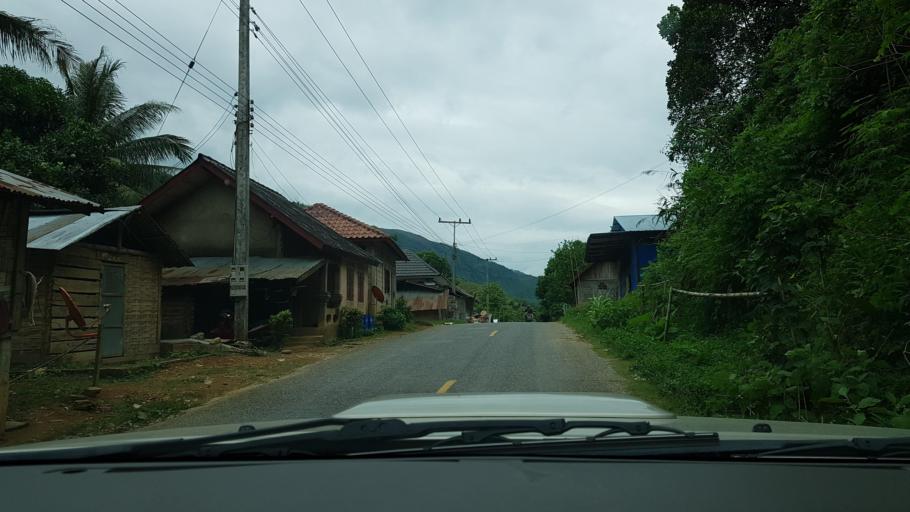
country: LA
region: Oudomxai
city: Muang La
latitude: 20.9816
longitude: 102.2252
